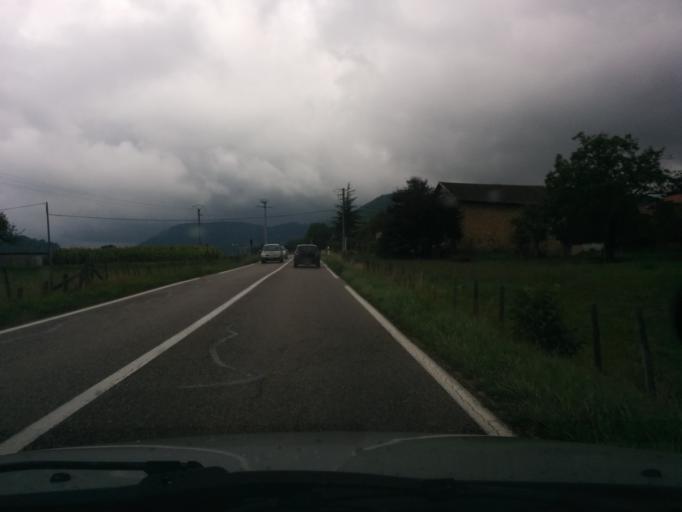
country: FR
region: Rhone-Alpes
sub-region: Departement de l'Isere
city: Saint-Geoire-en-Valdaine
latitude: 45.4394
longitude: 5.5997
